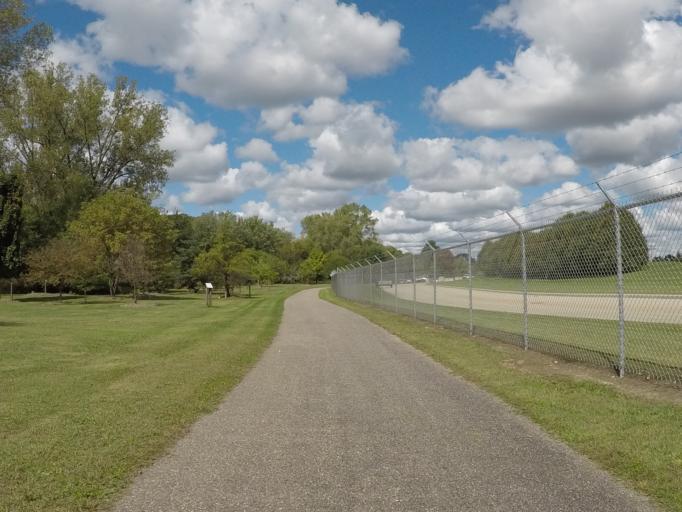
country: US
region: Wisconsin
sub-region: Richland County
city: Richland Center
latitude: 43.3312
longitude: -90.3891
